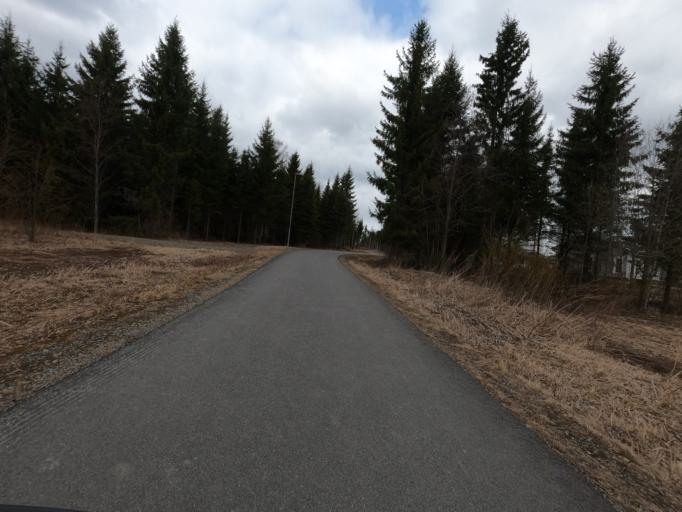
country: FI
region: North Karelia
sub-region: Joensuu
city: Joensuu
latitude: 62.5623
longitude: 29.8219
